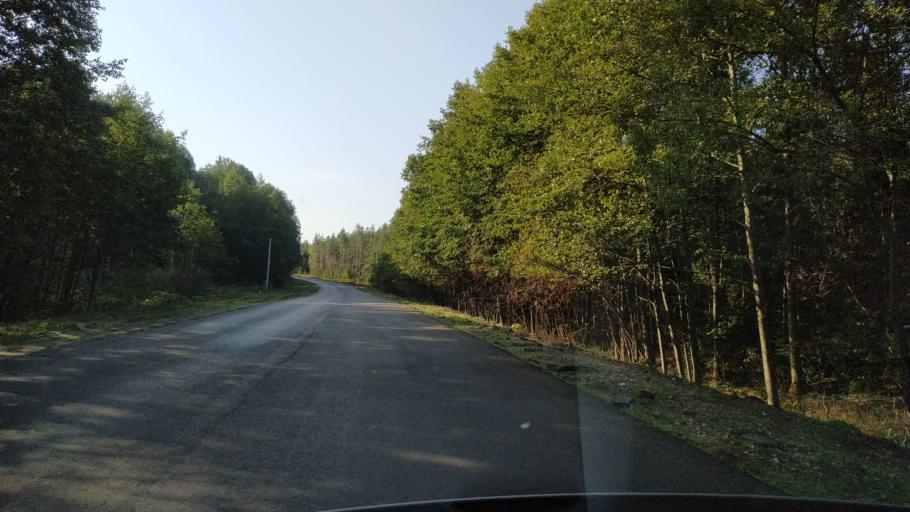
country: RU
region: Moskovskaya
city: Dmitrovskiy Pogost
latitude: 55.4148
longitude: 39.7490
